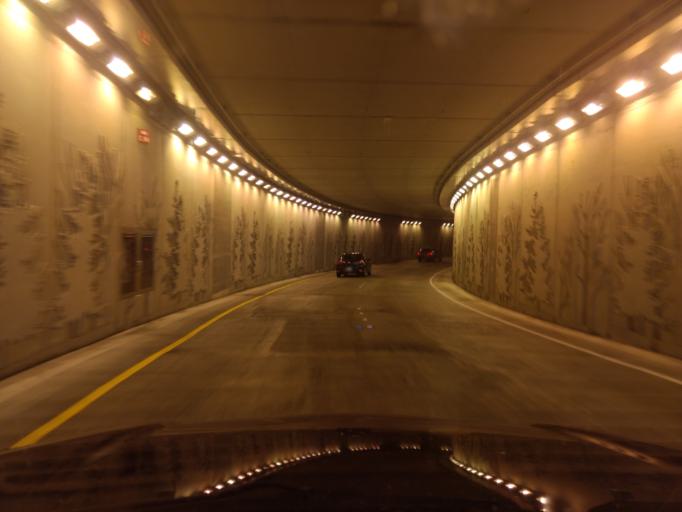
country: US
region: Washington
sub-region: Kitsap County
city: Bremerton
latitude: 47.5635
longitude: -122.6261
